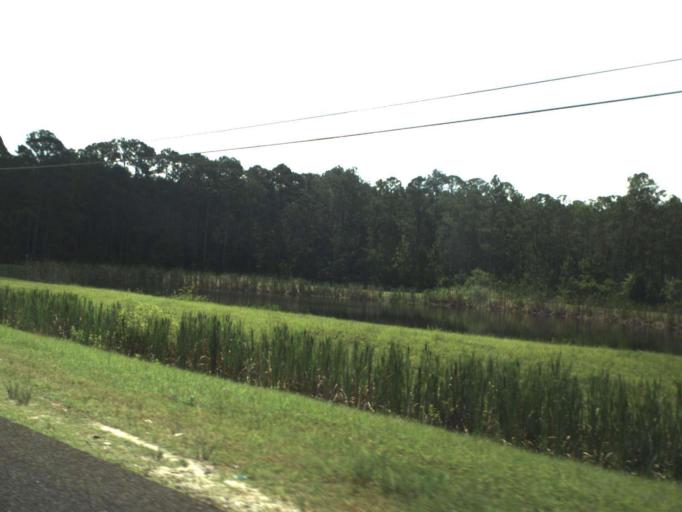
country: US
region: Florida
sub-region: Volusia County
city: Lake Helen
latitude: 29.0192
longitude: -81.2158
